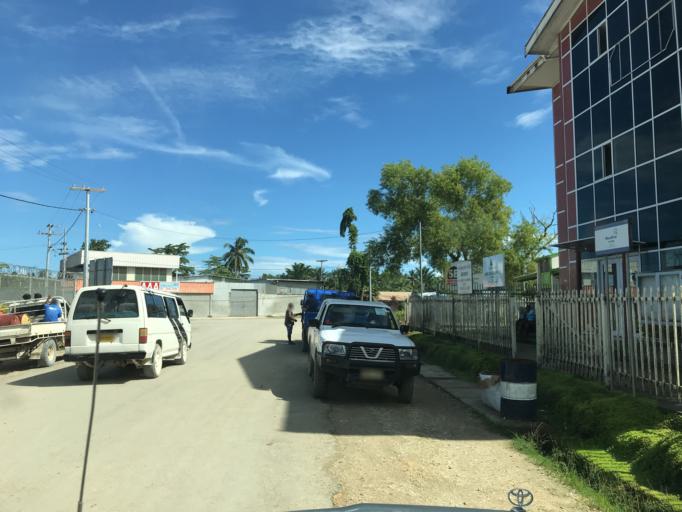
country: SB
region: Malaita
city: Auki
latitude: -8.7716
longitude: 160.6977
